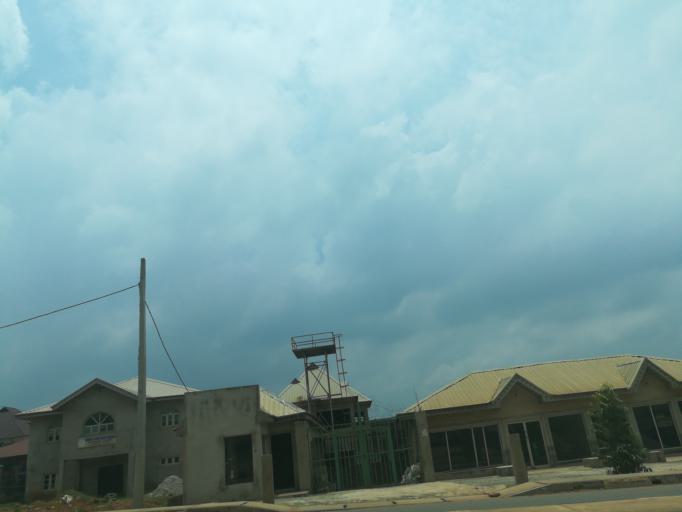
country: NG
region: Lagos
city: Ikorodu
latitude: 6.6304
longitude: 3.5332
